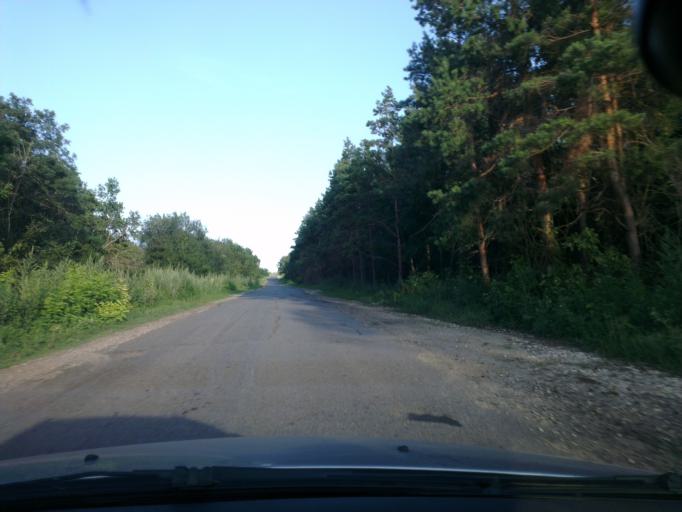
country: MD
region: Cantemir
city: Iargara
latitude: 46.3688
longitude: 28.3840
